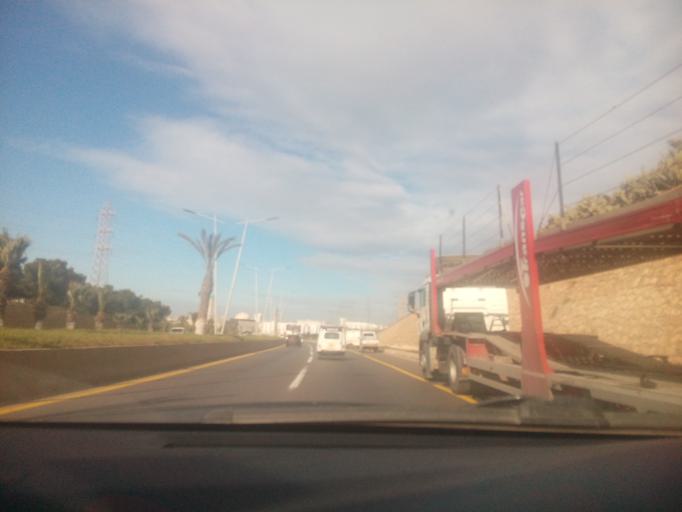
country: DZ
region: Oran
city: Es Senia
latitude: 35.6734
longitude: -0.5962
